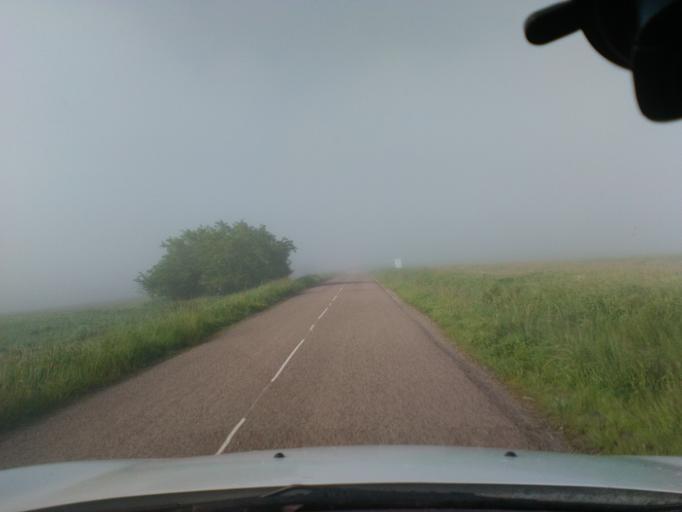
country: FR
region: Lorraine
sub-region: Departement des Vosges
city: Charmes
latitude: 48.3443
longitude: 6.2378
